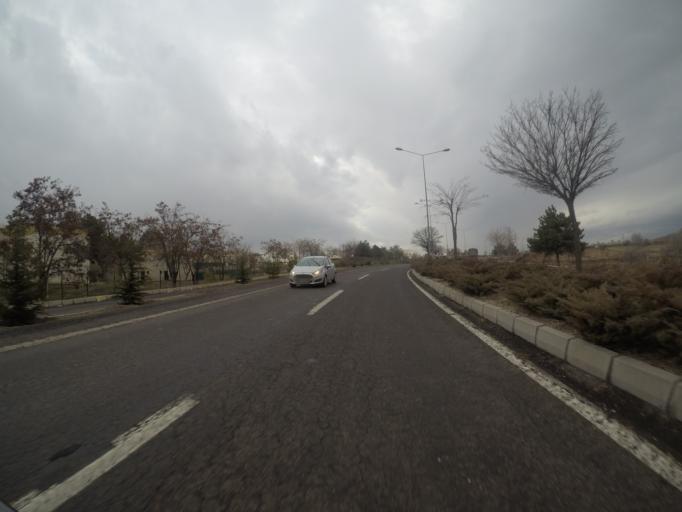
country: TR
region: Nevsehir
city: Urgub
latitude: 38.6352
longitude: 34.9007
